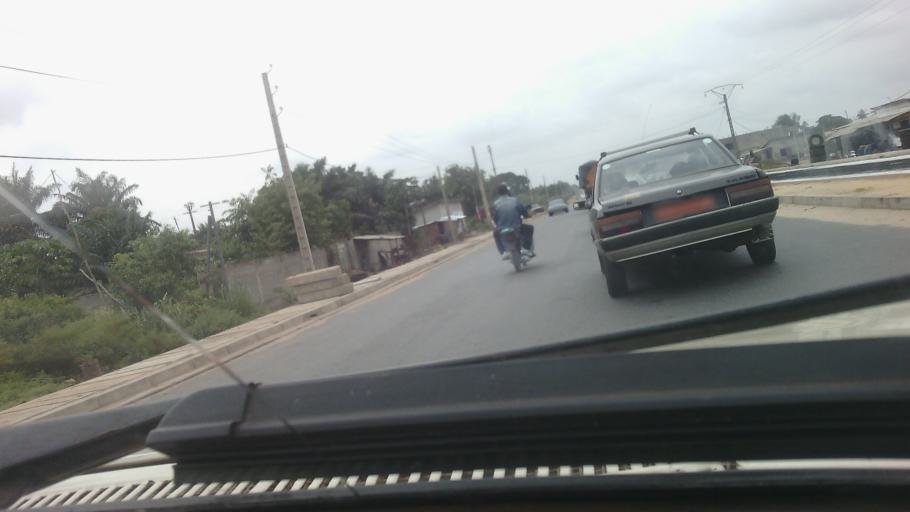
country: BJ
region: Atlantique
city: Hevie
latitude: 6.3826
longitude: 2.1791
